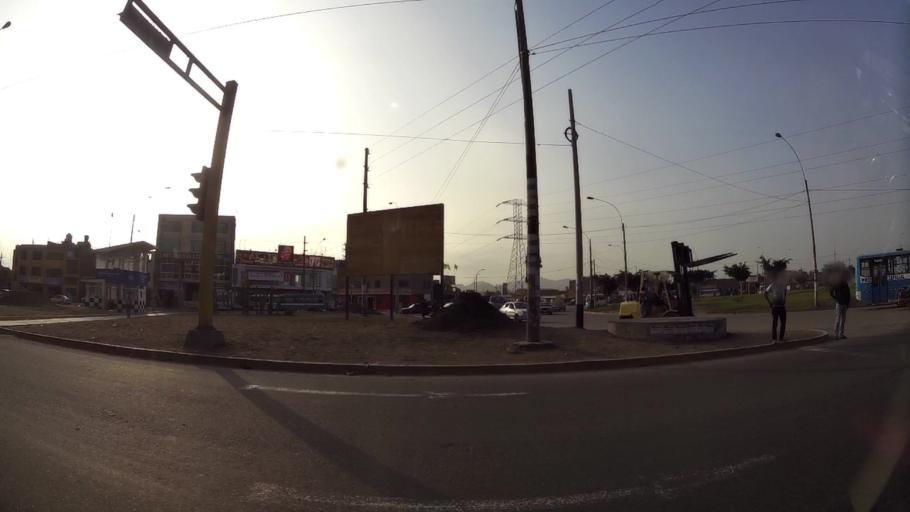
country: PE
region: Lima
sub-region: Lima
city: Independencia
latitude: -11.9744
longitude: -77.0882
